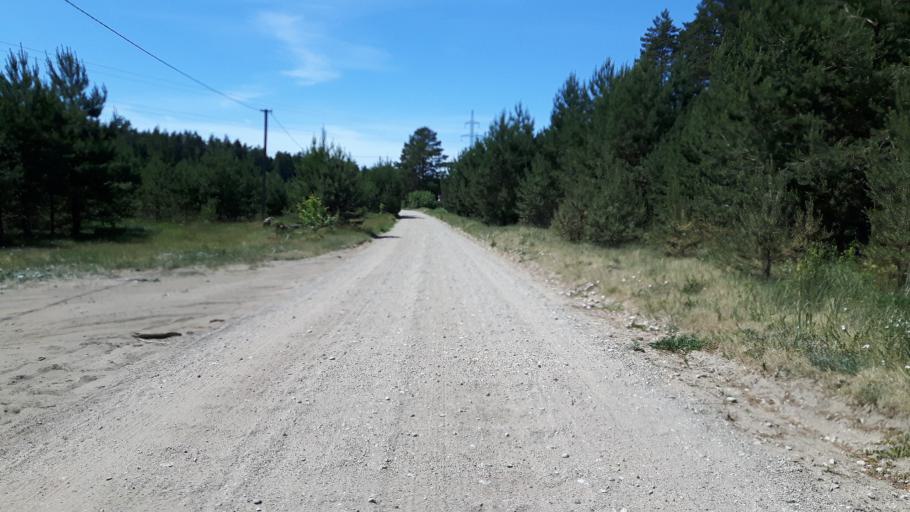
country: LV
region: Kandava
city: Kandava
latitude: 57.0409
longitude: 22.8126
